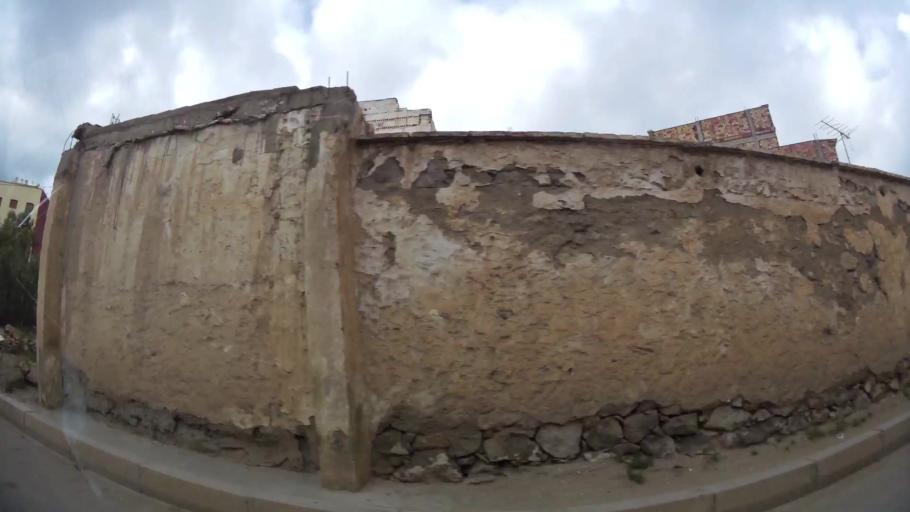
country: MA
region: Oriental
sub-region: Nador
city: Nador
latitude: 35.1602
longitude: -2.9393
